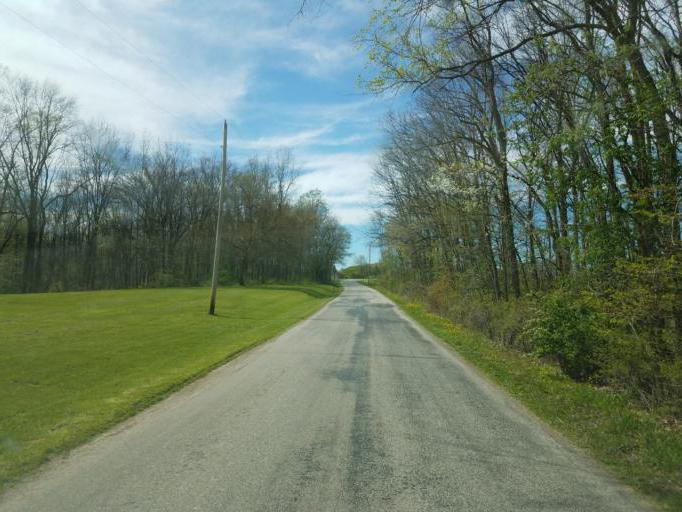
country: US
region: Ohio
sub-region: Richland County
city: Lincoln Heights
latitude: 40.8942
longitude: -82.5145
